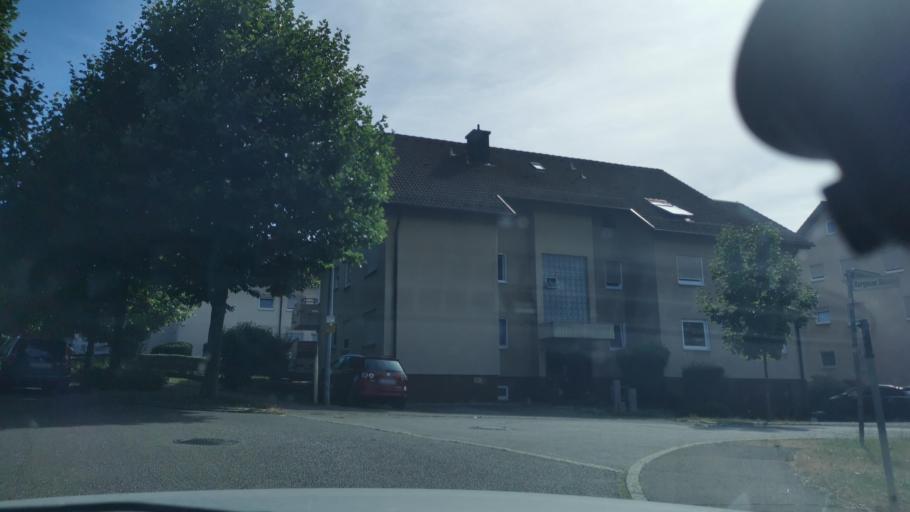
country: DE
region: Baden-Wuerttemberg
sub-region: Regierungsbezirk Stuttgart
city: Heubach
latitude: 48.7961
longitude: 9.9222
